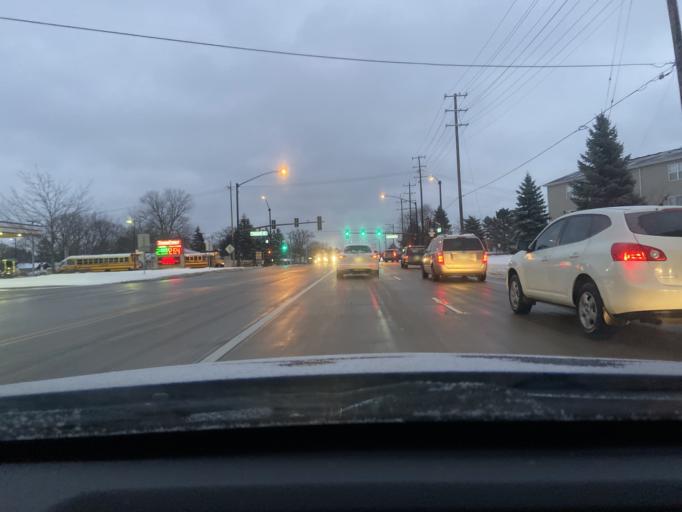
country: US
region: Illinois
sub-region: Lake County
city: Round Lake Park
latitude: 42.3570
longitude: -88.0691
